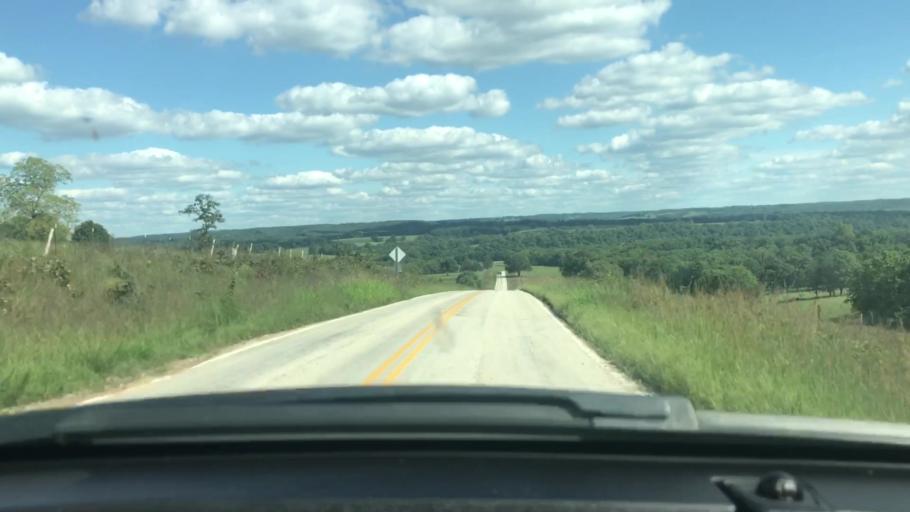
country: US
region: Missouri
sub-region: Wright County
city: Hartville
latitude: 37.3762
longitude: -92.4067
